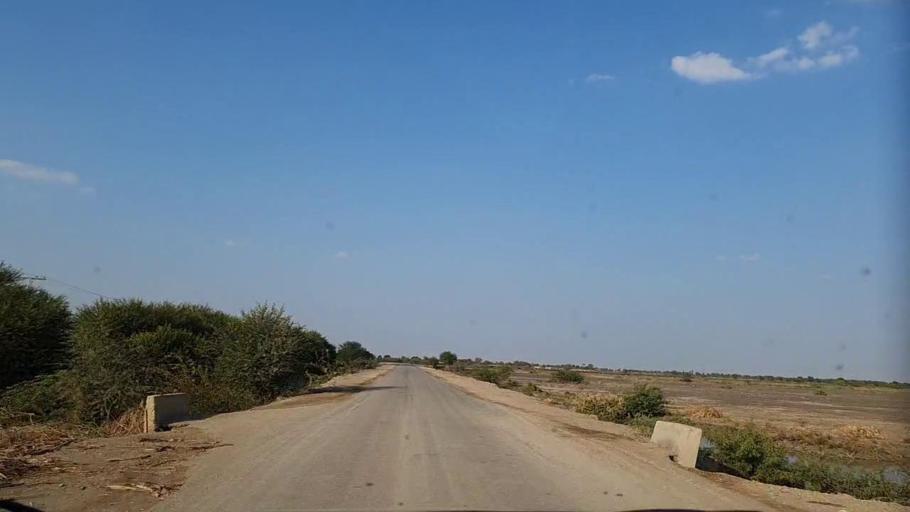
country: PK
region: Sindh
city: Pithoro
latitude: 25.6957
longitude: 69.2225
